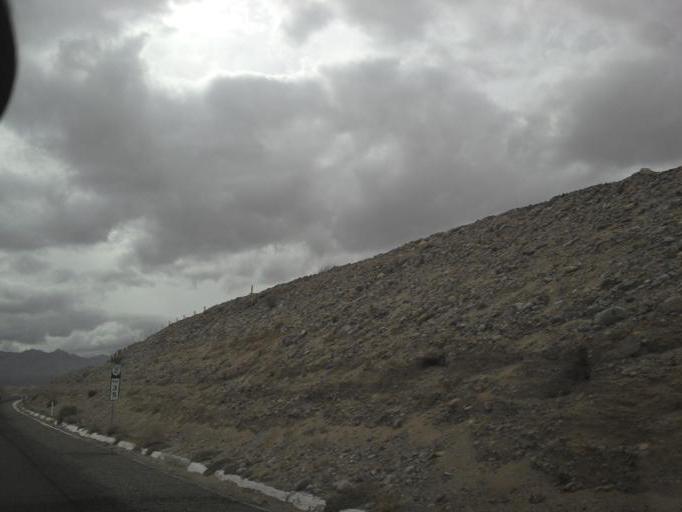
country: MX
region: Baja California
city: Progreso
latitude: 32.5646
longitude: -115.8655
